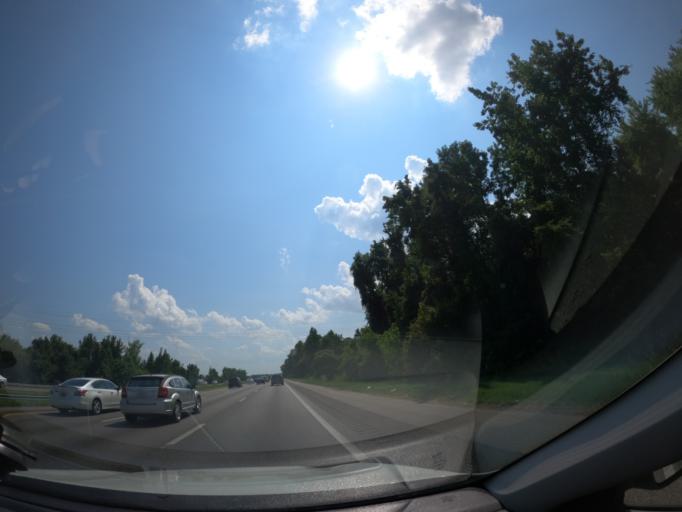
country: US
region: South Carolina
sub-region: Richland County
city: Columbia
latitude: 33.9467
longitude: -80.9992
